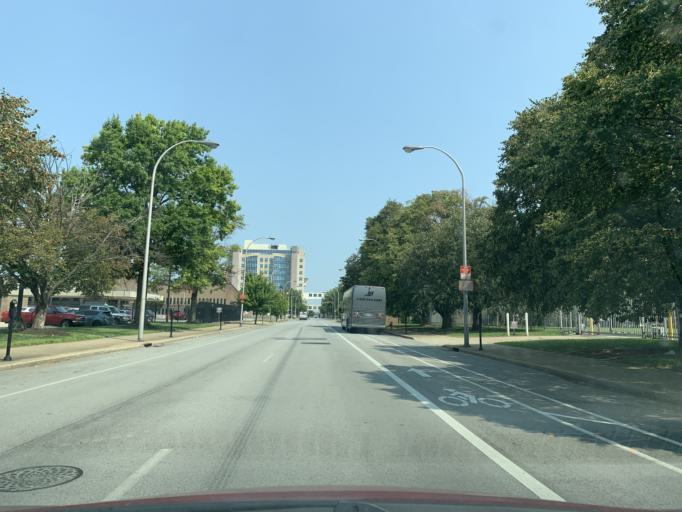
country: US
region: Kentucky
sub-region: Jefferson County
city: Louisville
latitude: 38.2502
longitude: -85.7627
